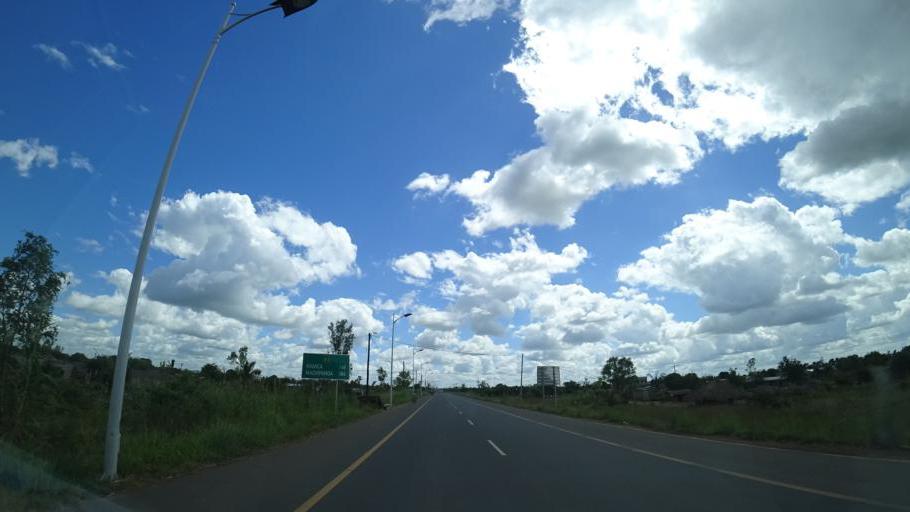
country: MZ
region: Sofala
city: Dondo
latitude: -19.2789
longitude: 34.2186
